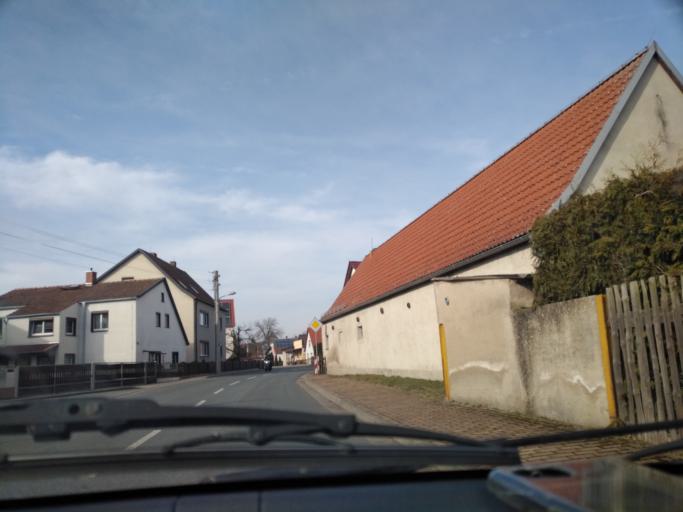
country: DE
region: Saxony
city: Nauwalde
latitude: 51.4260
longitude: 13.3605
